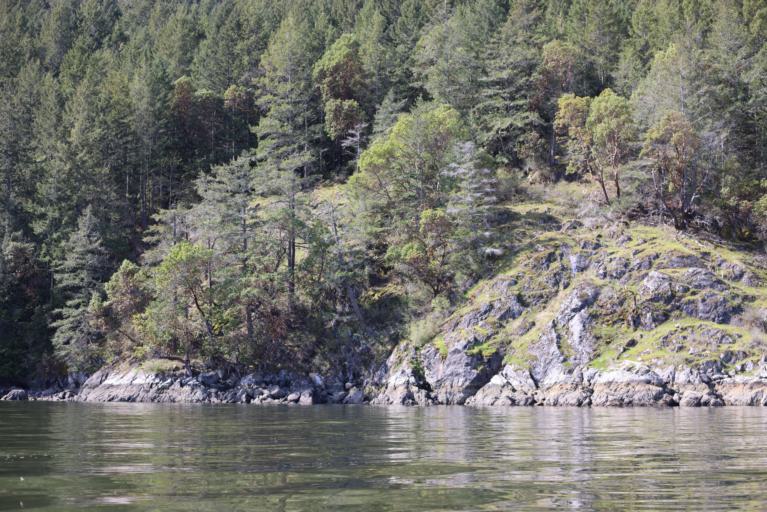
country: CA
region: British Columbia
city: Langford
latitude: 48.5774
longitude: -123.5174
